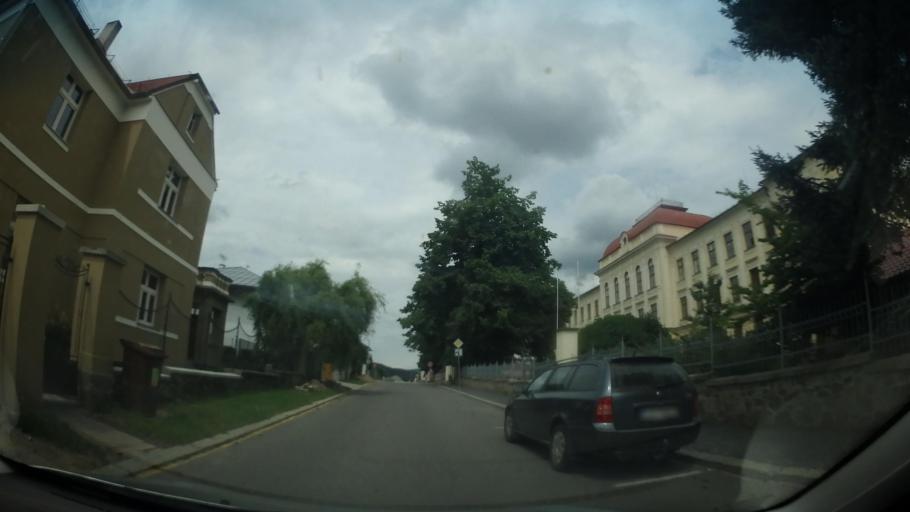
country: CZ
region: Vysocina
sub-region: Okres Zd'ar nad Sazavou
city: Nove Mesto na Morave
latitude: 49.5631
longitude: 16.0728
